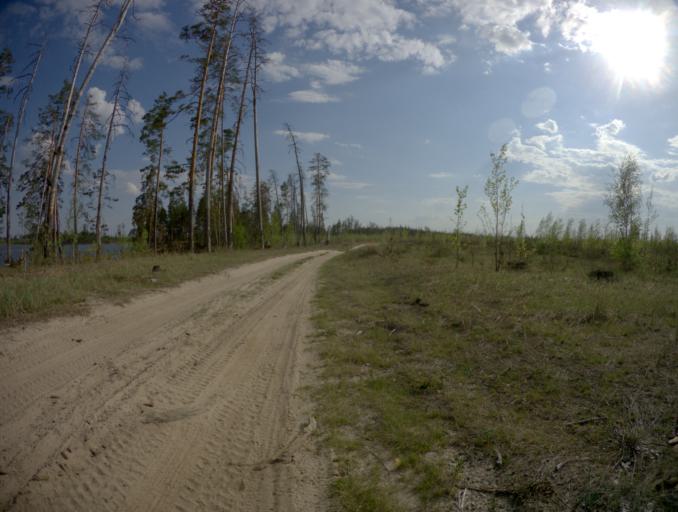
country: RU
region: Ivanovo
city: Talitsy
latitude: 56.4172
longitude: 42.2770
